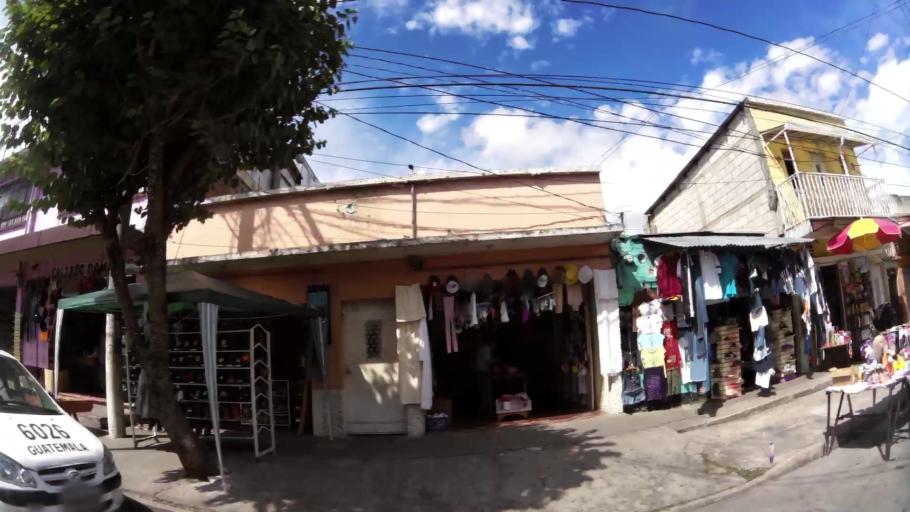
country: GT
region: Guatemala
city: Mixco
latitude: 14.6559
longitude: -90.5790
